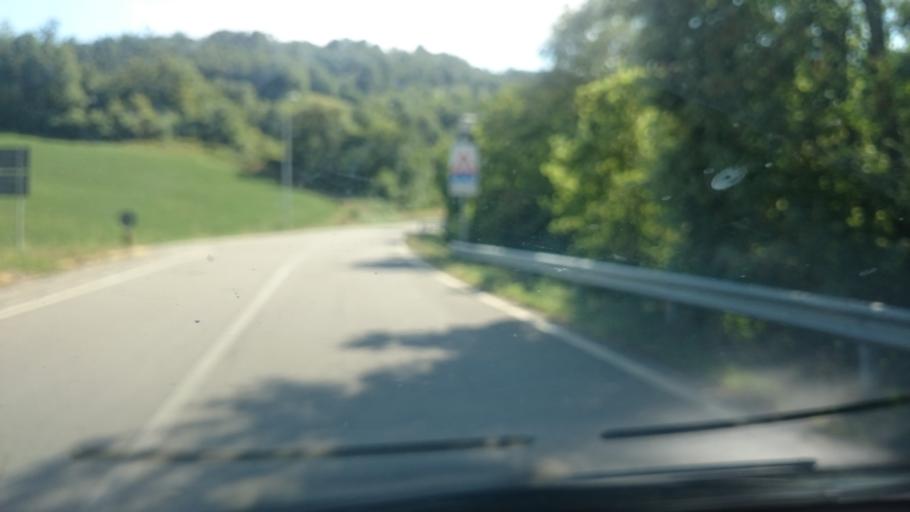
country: IT
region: Emilia-Romagna
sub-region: Provincia di Reggio Emilia
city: Carpineti
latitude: 44.4083
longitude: 10.5231
